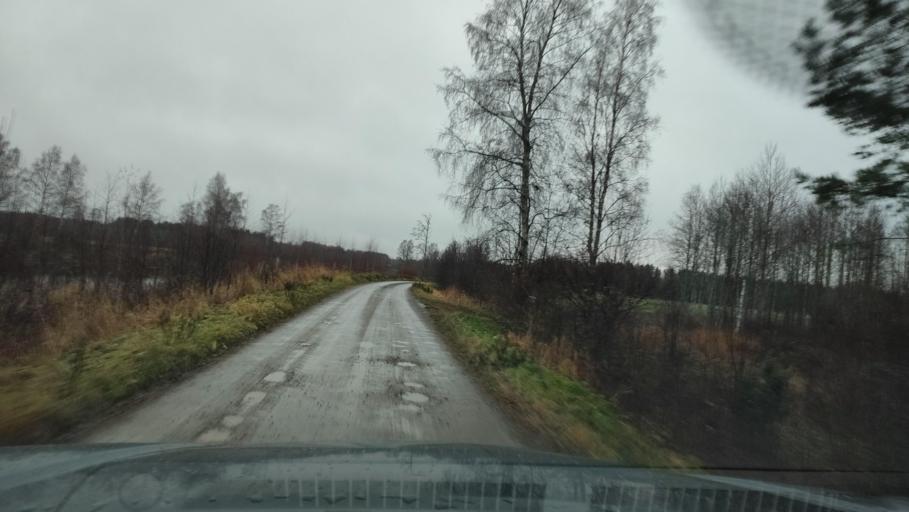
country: FI
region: Ostrobothnia
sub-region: Sydosterbotten
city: Kristinestad
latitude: 62.2349
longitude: 21.4589
